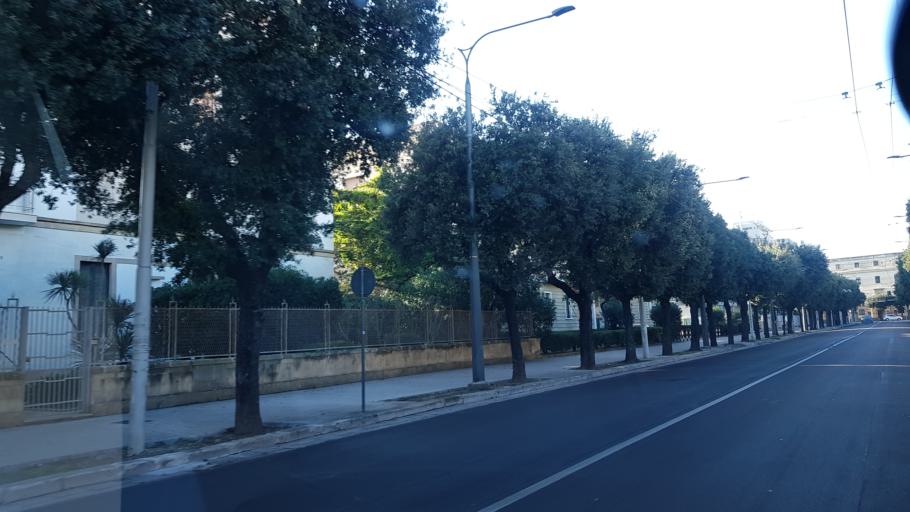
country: IT
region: Apulia
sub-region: Provincia di Lecce
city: Lecce
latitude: 40.3495
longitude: 18.1655
